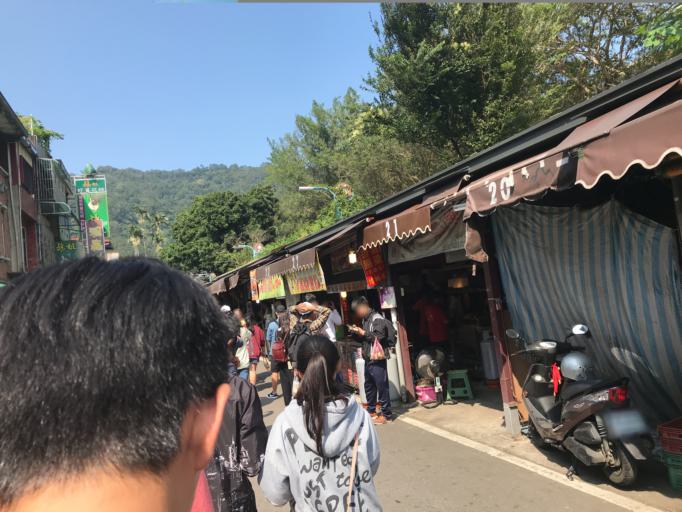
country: TW
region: Taiwan
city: Daxi
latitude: 24.7041
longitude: 121.1831
